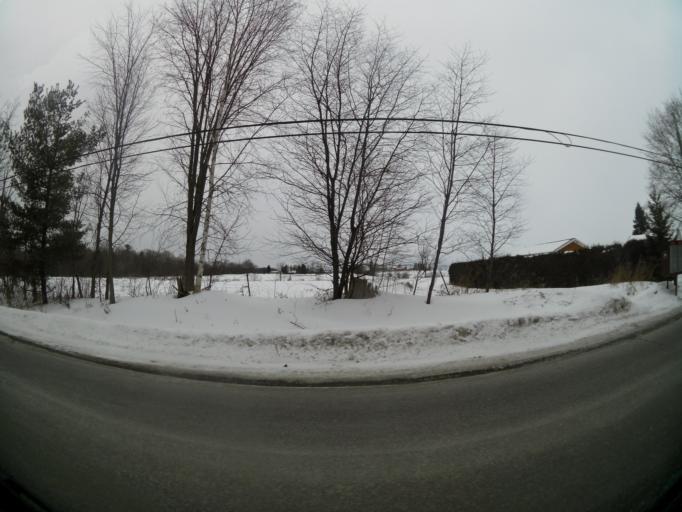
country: CA
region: Ontario
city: Clarence-Rockland
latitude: 45.4203
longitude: -75.4294
